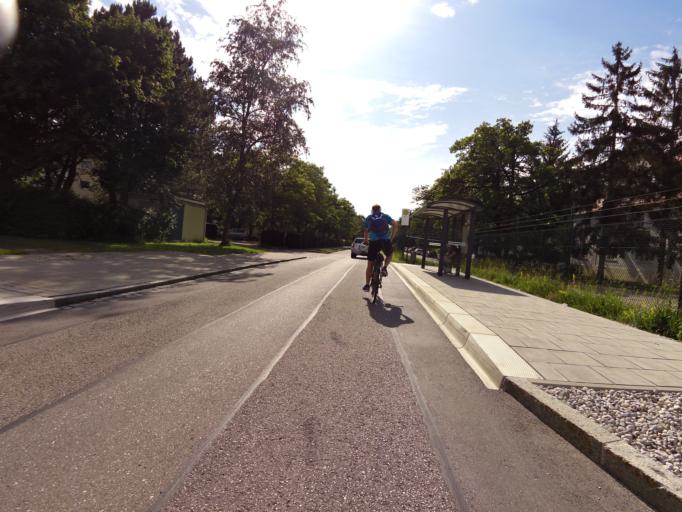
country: DE
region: Bavaria
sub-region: Upper Bavaria
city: Hebertshausen
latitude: 48.2669
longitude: 11.4590
